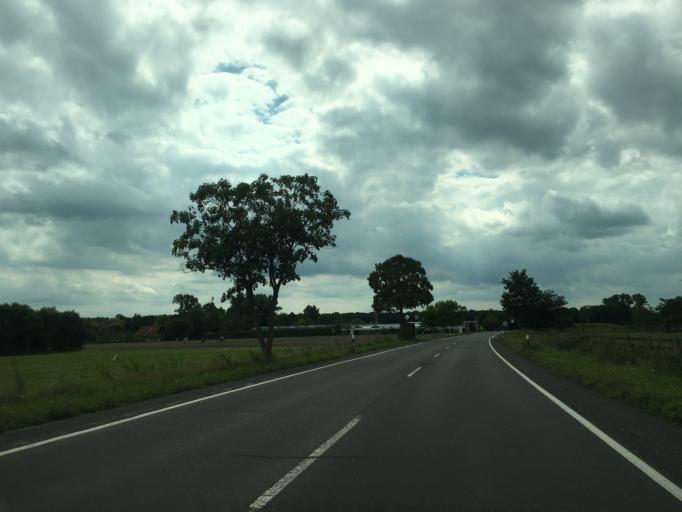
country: DE
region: North Rhine-Westphalia
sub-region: Regierungsbezirk Munster
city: Nordkirchen
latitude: 51.7288
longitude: 7.5130
